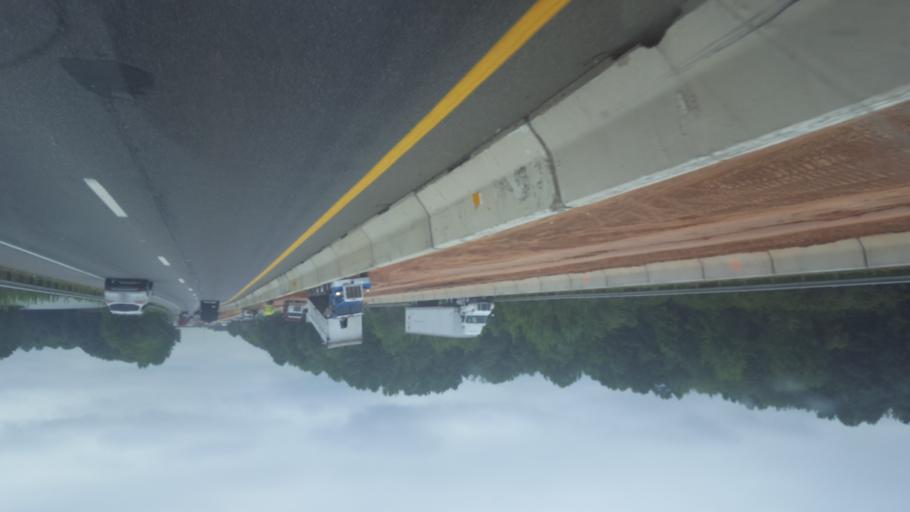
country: US
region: North Carolina
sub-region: Gaston County
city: Davidson
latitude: 35.5167
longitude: -80.8652
